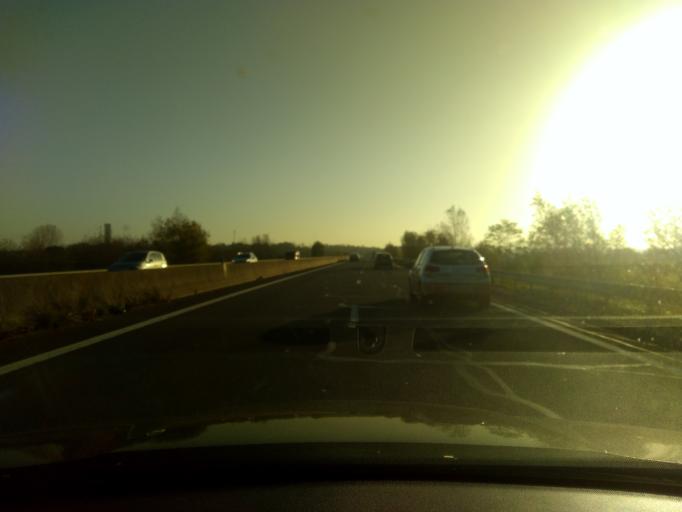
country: FR
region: Lorraine
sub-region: Departement de la Moselle
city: Marly
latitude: 49.0516
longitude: 6.1538
